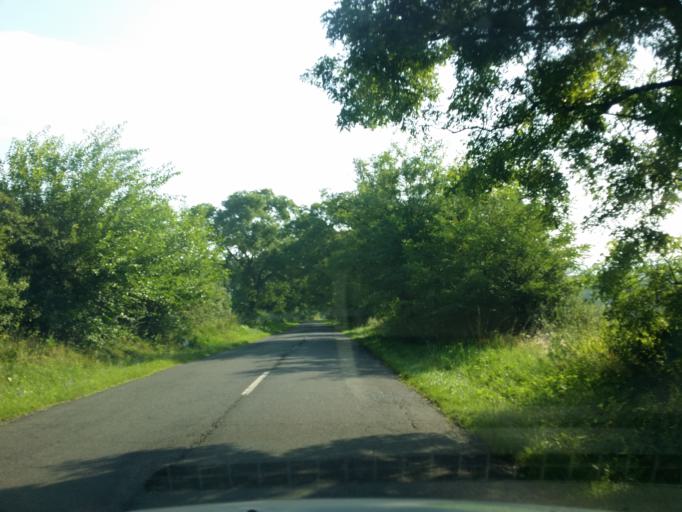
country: HU
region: Borsod-Abauj-Zemplen
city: Abaujszanto
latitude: 48.3661
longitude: 21.2220
